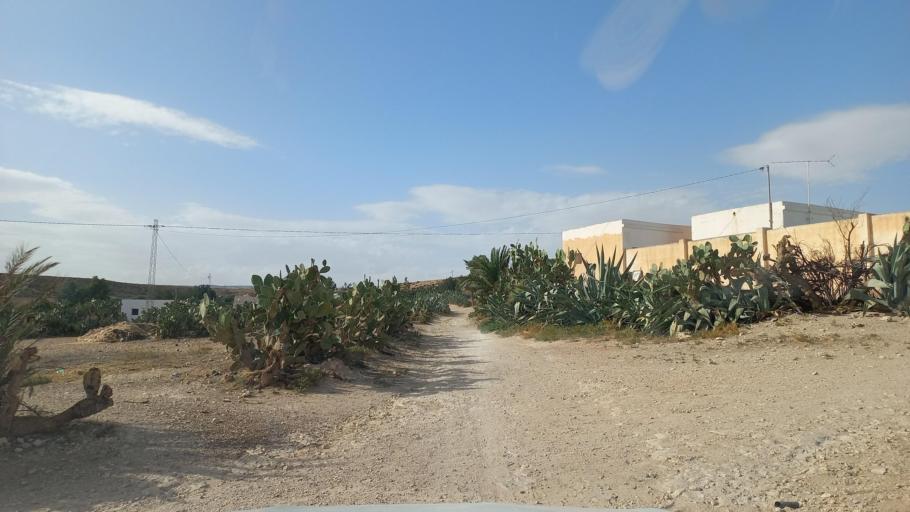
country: TN
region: Al Qasrayn
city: Kasserine
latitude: 35.2569
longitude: 8.9297
